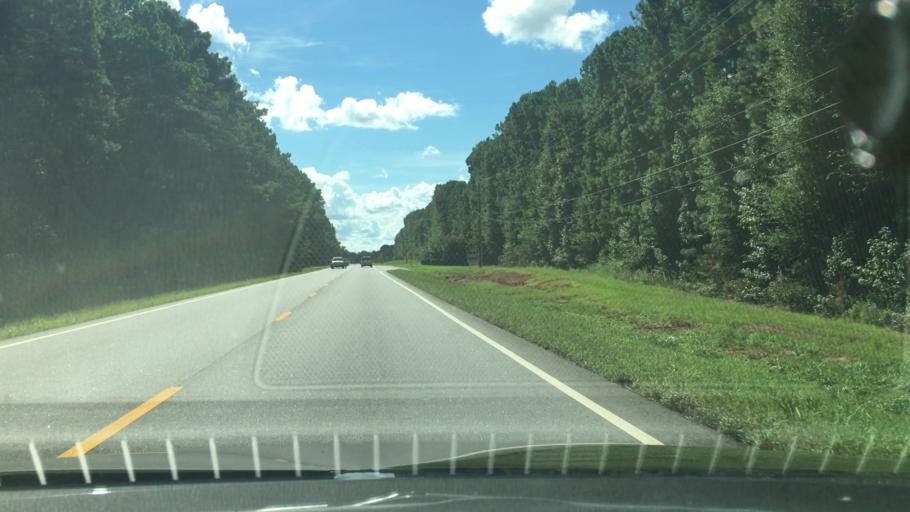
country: US
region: Georgia
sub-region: Butts County
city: Jackson
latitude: 33.2908
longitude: -84.0081
